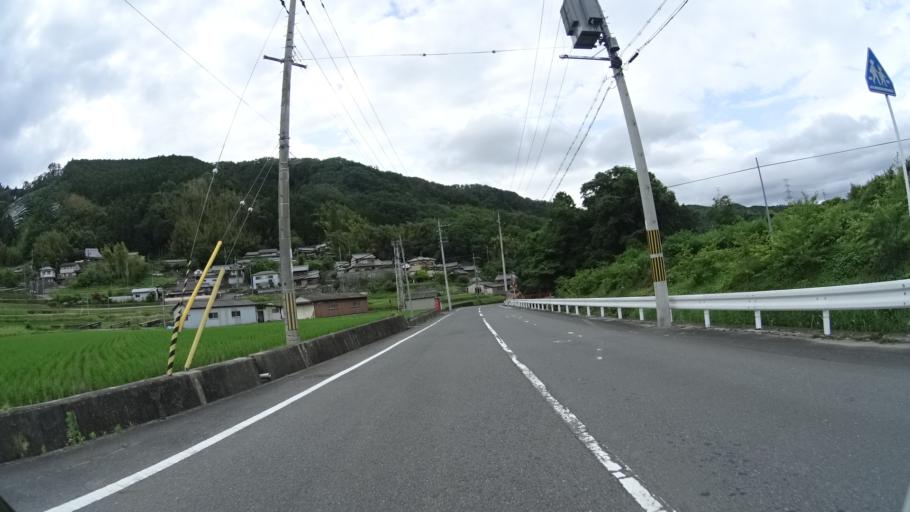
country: JP
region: Nara
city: Nara-shi
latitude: 34.7389
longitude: 135.9144
